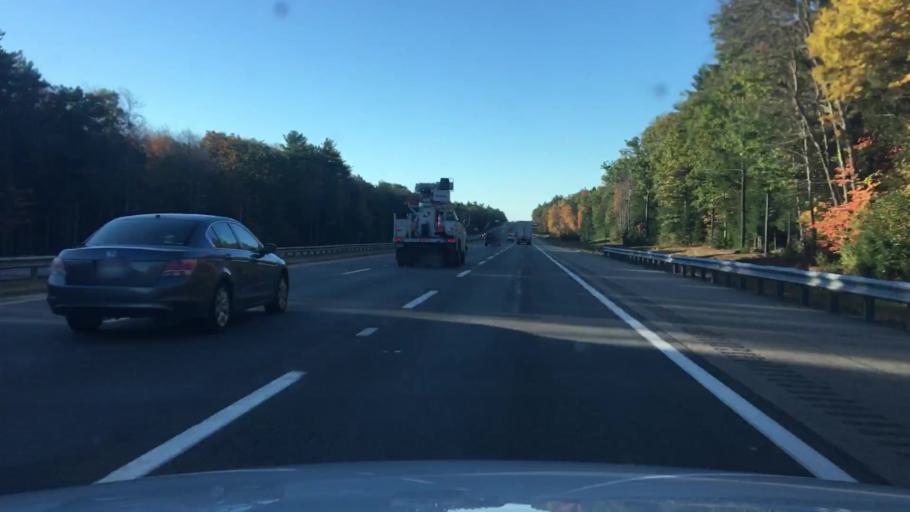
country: US
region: Maine
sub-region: York County
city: Wells Beach Station
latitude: 43.2936
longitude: -70.6165
